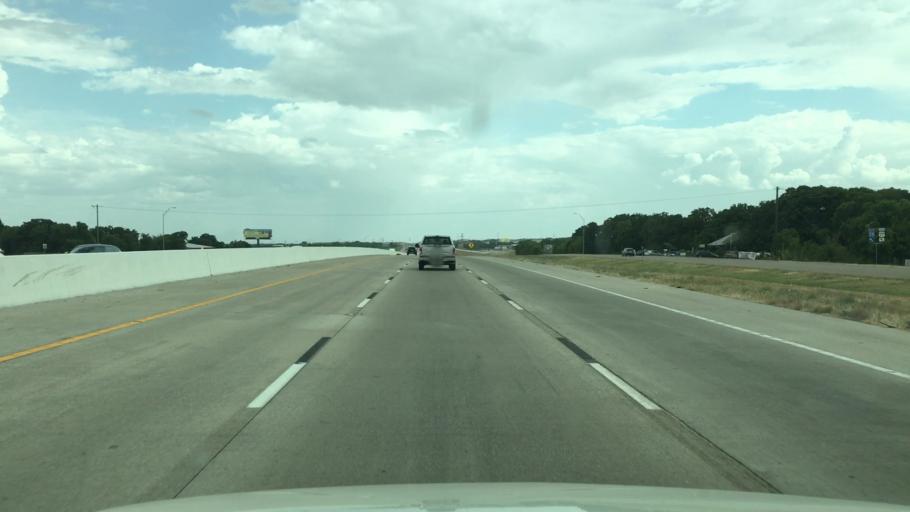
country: US
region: Texas
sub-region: McLennan County
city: West
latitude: 31.7376
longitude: -97.1035
